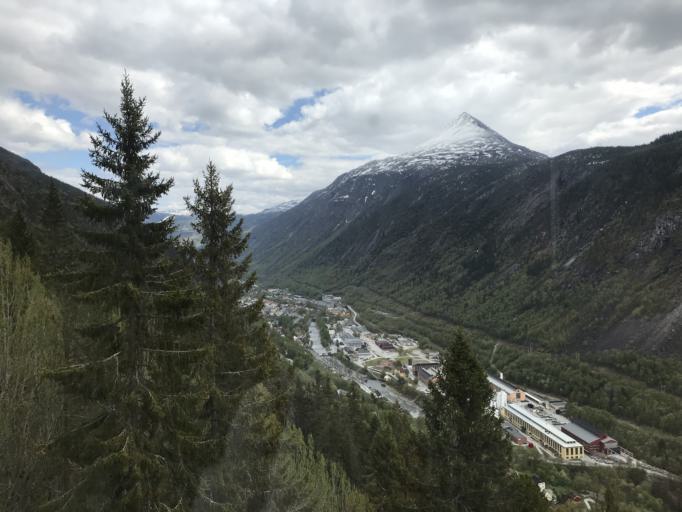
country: NO
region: Telemark
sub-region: Tinn
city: Rjukan
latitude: 59.8824
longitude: 8.5513
